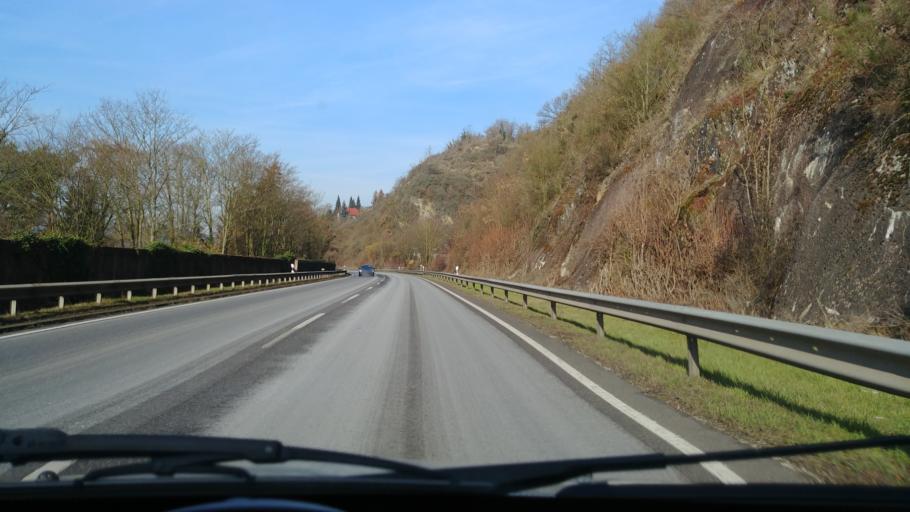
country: DE
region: Rheinland-Pfalz
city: Lahnstein
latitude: 50.2955
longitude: 7.6205
